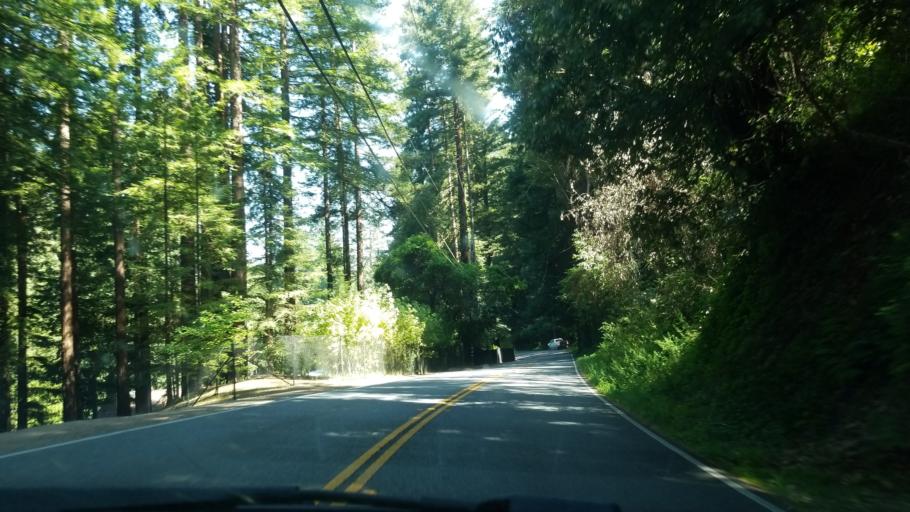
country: US
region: California
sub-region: Santa Cruz County
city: Scotts Valley
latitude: 37.0826
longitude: -121.9481
